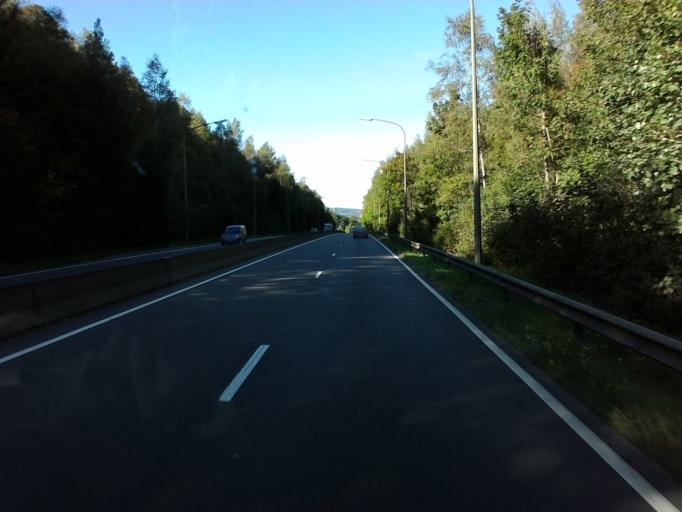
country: BE
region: Wallonia
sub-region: Province du Luxembourg
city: Messancy
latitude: 49.5921
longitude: 5.8082
